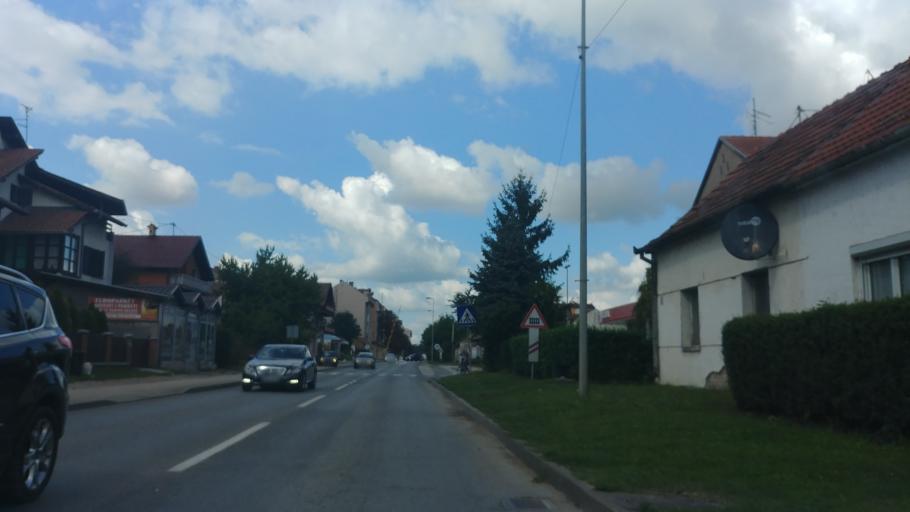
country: BA
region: Brcko
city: Brcko
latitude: 44.8688
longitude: 18.8184
